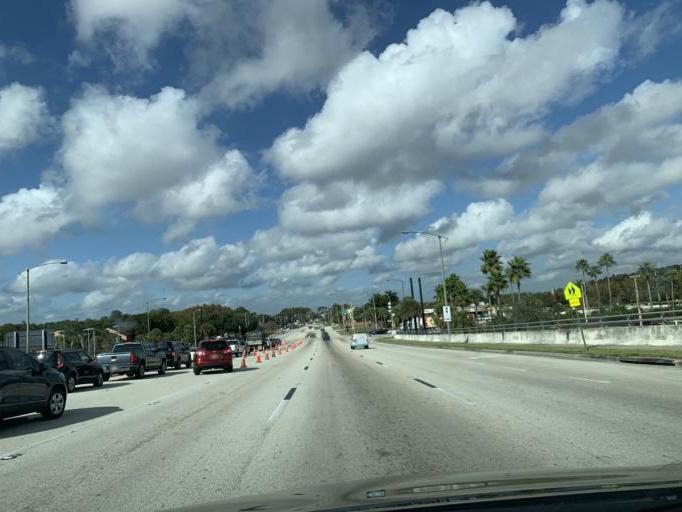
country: US
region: Florida
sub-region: Orange County
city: Oak Ridge
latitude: 28.4941
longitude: -81.4343
